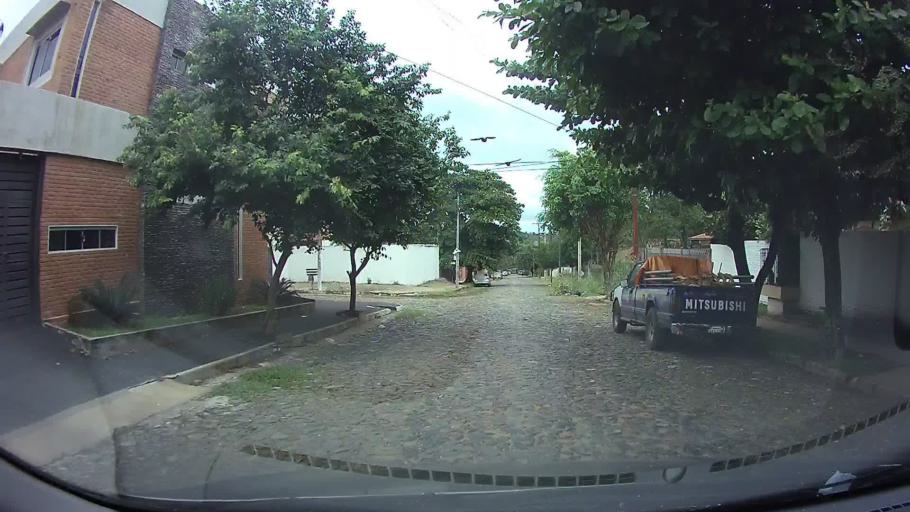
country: PY
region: Asuncion
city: Asuncion
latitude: -25.3181
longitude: -57.6179
